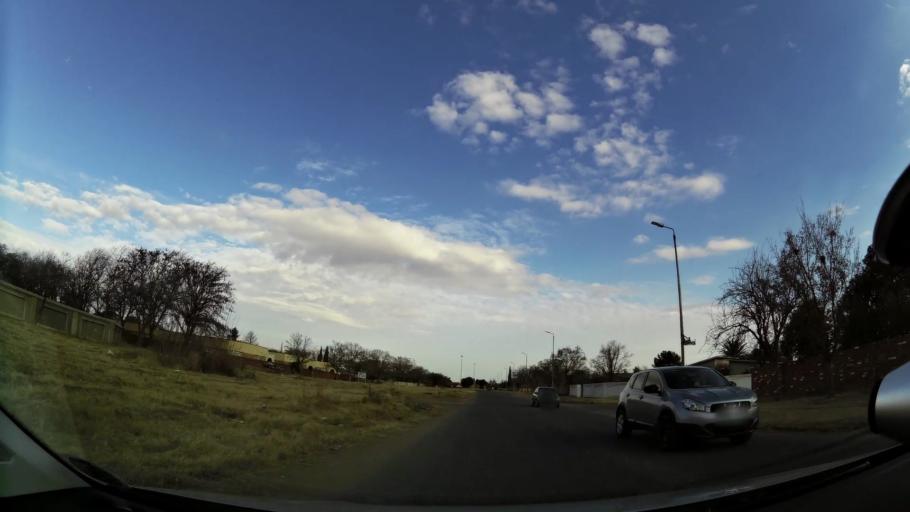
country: ZA
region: Orange Free State
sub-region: Lejweleputswa District Municipality
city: Welkom
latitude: -27.9835
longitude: 26.7118
